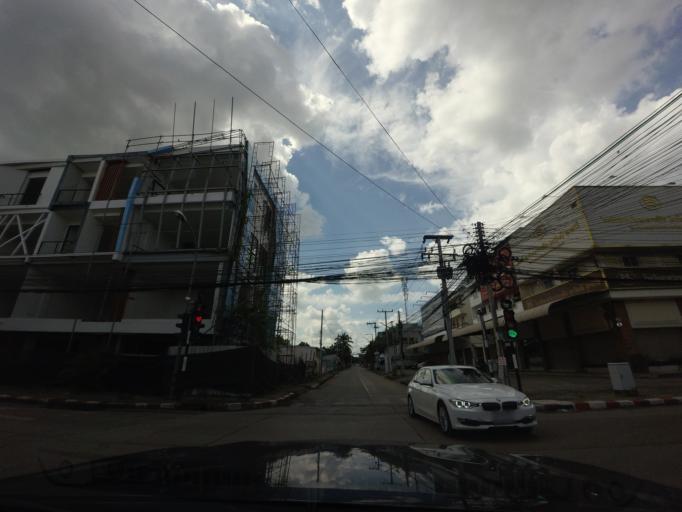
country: TH
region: Changwat Udon Thani
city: Udon Thani
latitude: 17.4109
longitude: 102.7759
